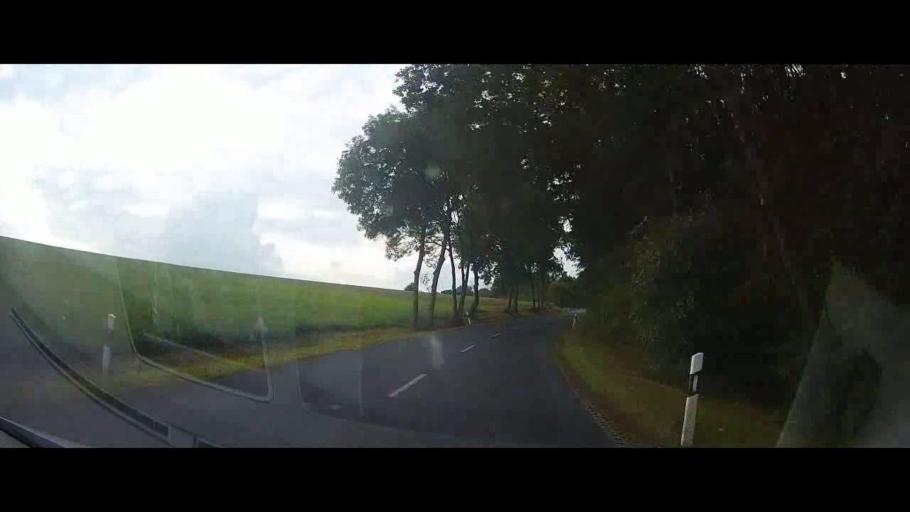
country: DE
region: Lower Saxony
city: Rosdorf
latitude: 51.5455
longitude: 9.8749
